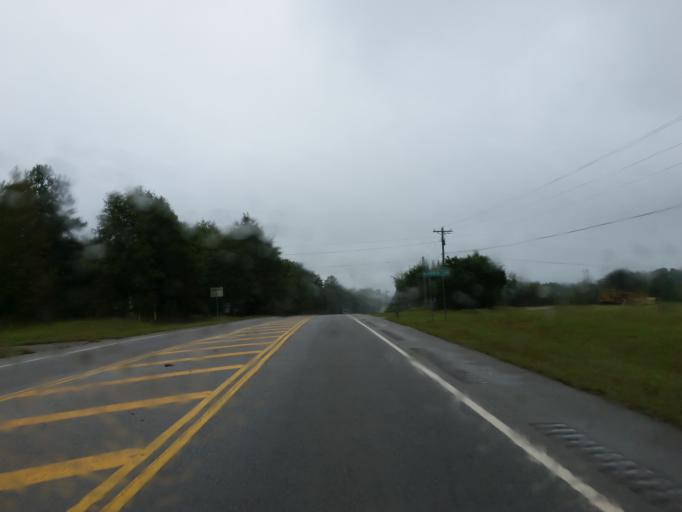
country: US
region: Georgia
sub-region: Lamar County
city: Barnesville
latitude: 33.0297
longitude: -84.1443
